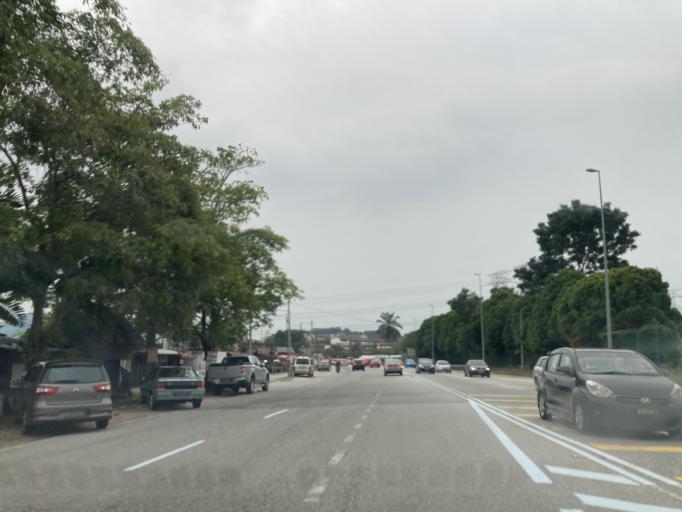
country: MY
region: Selangor
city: Kampung Baru Subang
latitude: 3.2023
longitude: 101.5468
